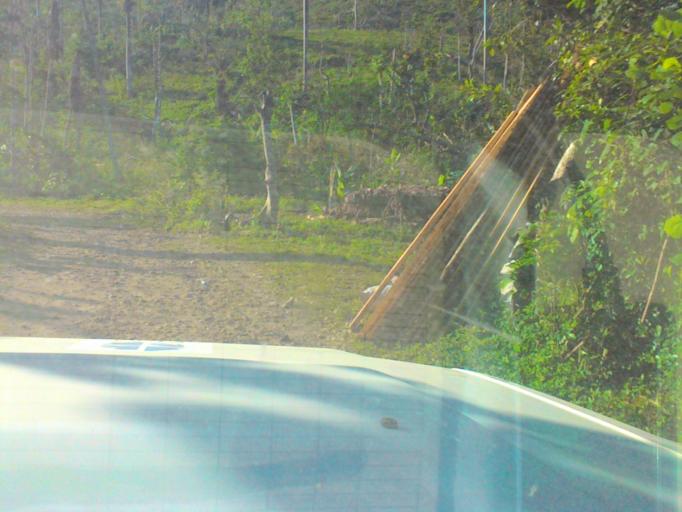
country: HT
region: Grandans
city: Jeremie
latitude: 18.5324
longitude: -74.0850
